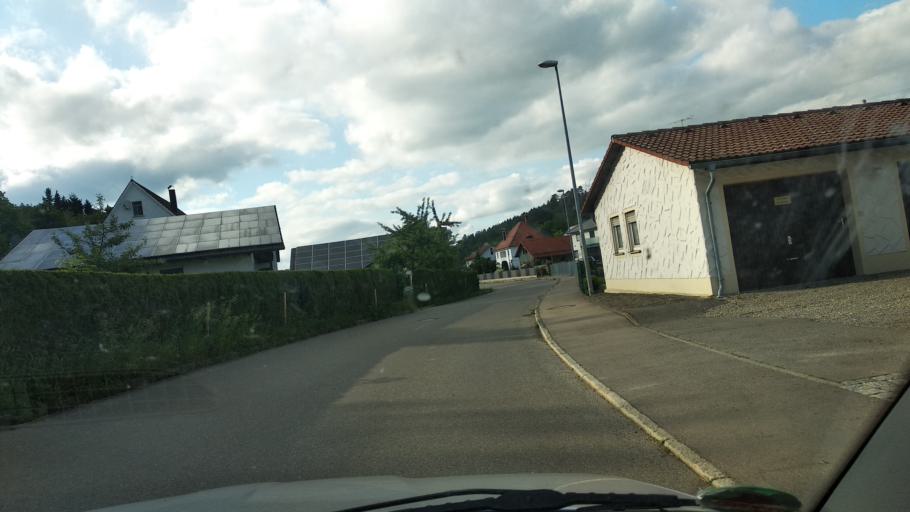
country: DE
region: Baden-Wuerttemberg
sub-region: Tuebingen Region
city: Rot an der Rot
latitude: 47.9762
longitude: 10.0469
